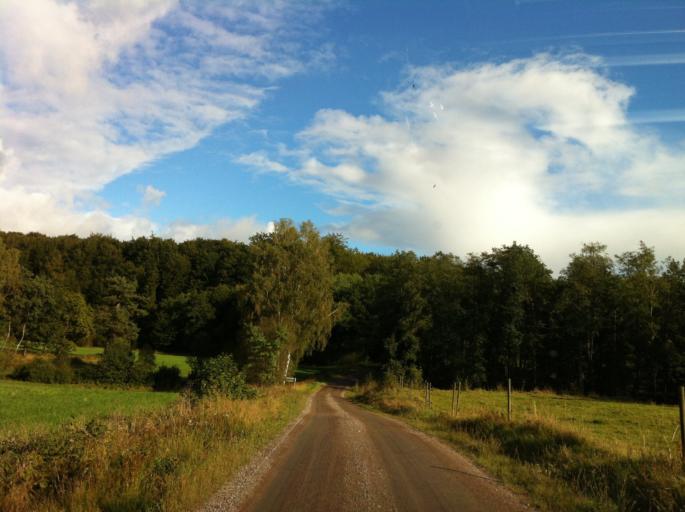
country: SE
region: Skane
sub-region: Perstorps Kommun
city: Perstorp
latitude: 56.1374
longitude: 13.5344
